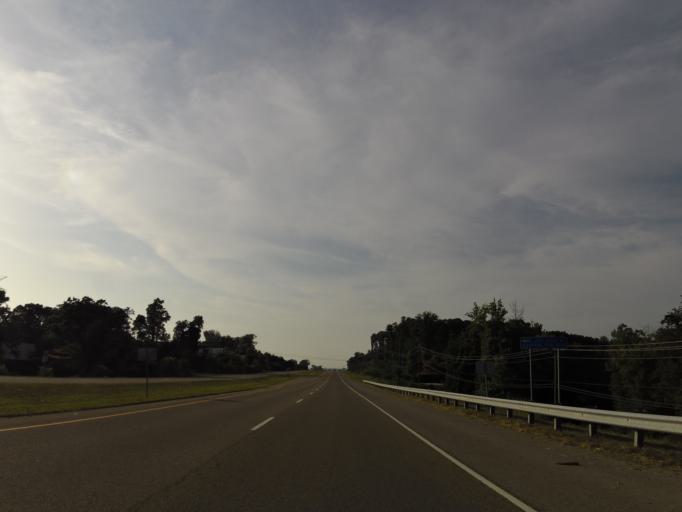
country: US
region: Tennessee
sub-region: Loudon County
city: Lenoir City
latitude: 35.7642
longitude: -84.2287
